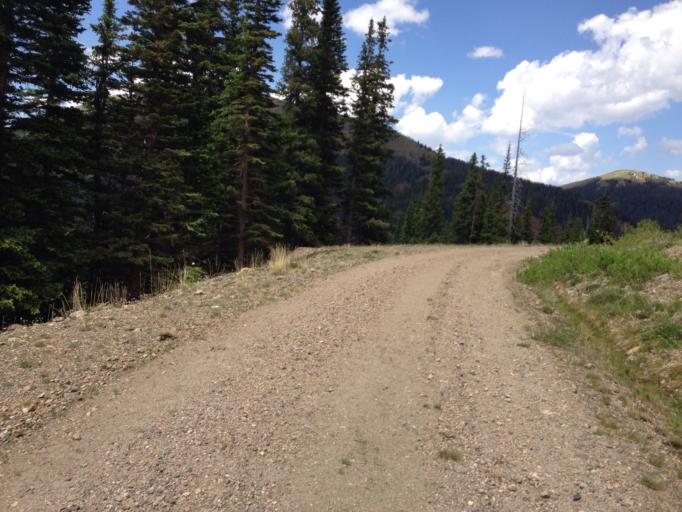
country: US
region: Colorado
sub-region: Larimer County
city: Estes Park
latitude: 40.4944
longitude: -105.8984
